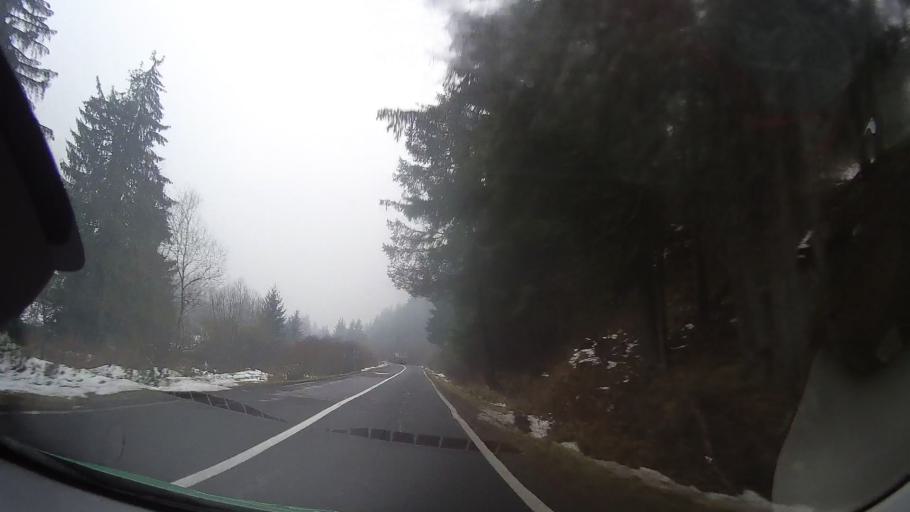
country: RO
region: Harghita
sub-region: Municipiul Gheorgheni
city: Gheorgheni
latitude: 46.7540
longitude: 25.6924
